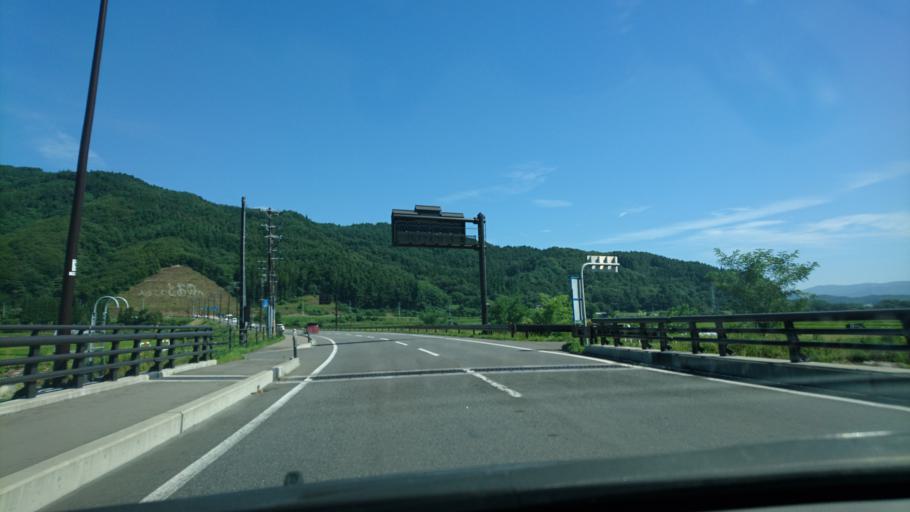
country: JP
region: Iwate
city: Tono
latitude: 39.3282
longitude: 141.5091
